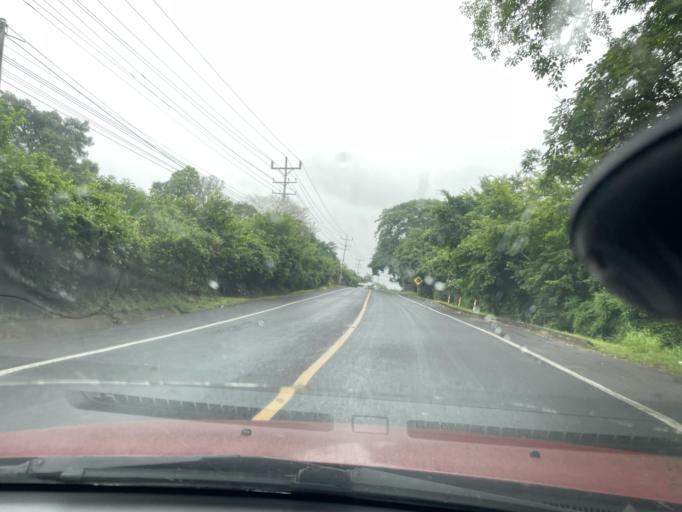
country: SV
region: San Miguel
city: San Miguel
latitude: 13.5293
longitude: -88.1404
